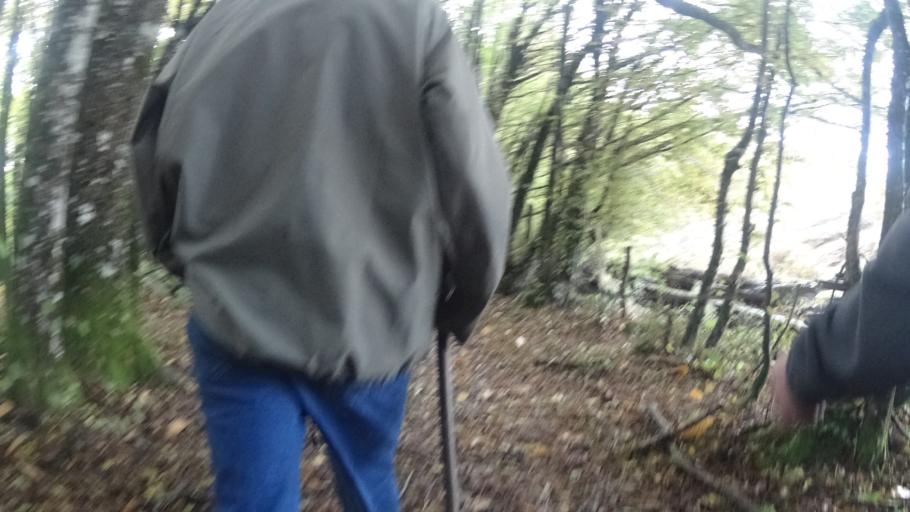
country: FR
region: Aquitaine
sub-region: Departement de la Dordogne
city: Payzac
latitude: 45.3575
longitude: 1.2108
